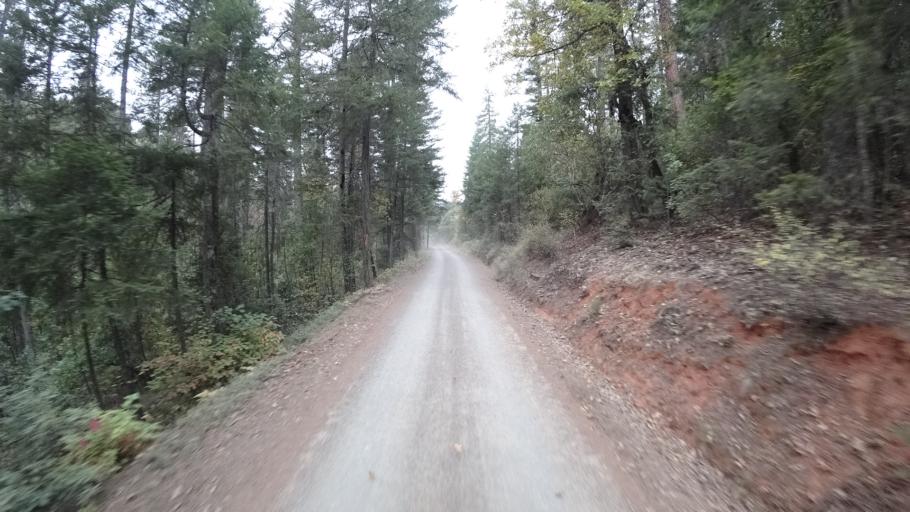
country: US
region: California
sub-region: Siskiyou County
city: Happy Camp
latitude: 41.7828
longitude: -123.3314
